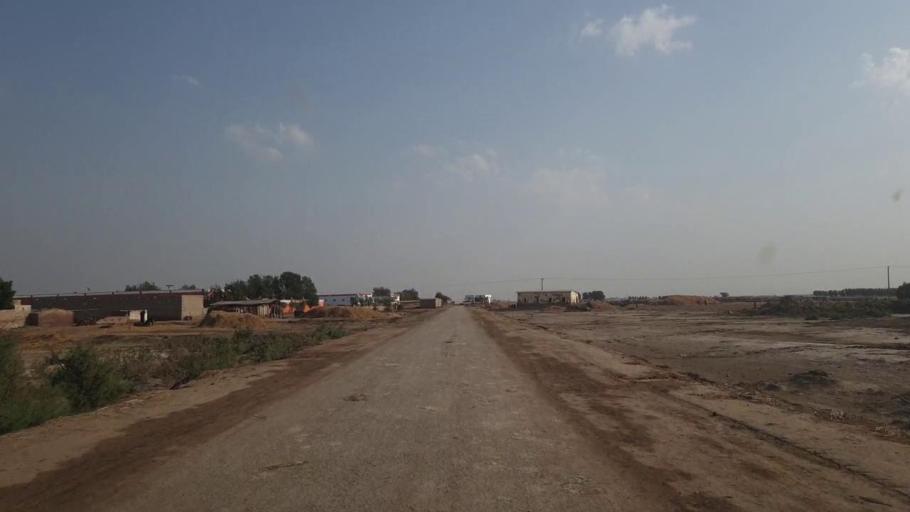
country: PK
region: Sindh
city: Kario
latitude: 24.5820
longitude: 68.5407
